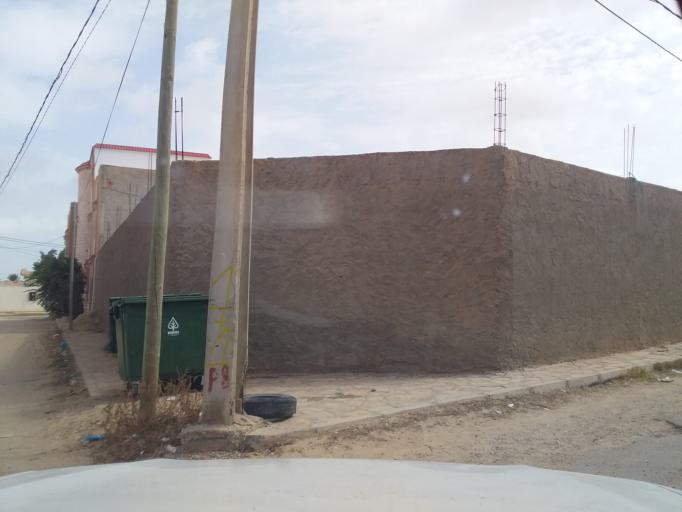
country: TN
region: Qabis
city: Gabes
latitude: 33.6189
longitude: 10.2931
